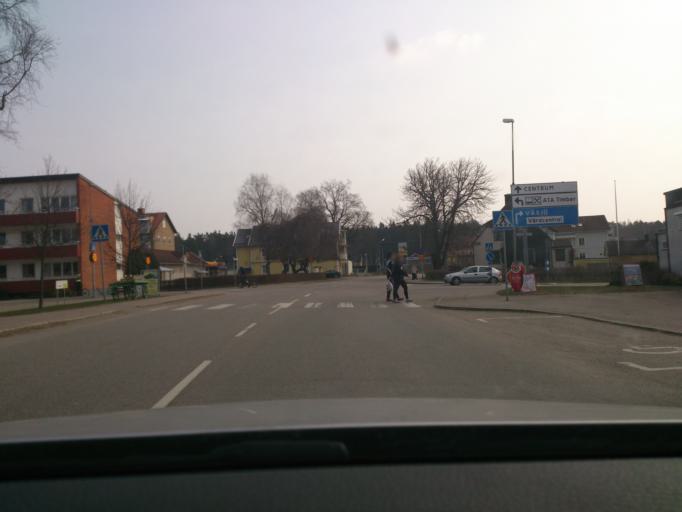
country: SE
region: Kronoberg
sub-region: Alvesta Kommun
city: Moheda
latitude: 57.0019
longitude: 14.5735
